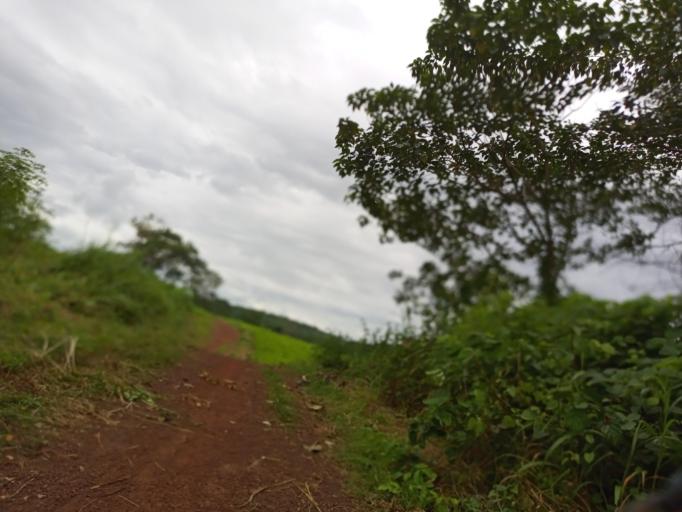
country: SL
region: Northern Province
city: Kamakwie
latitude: 9.5054
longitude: -12.2630
